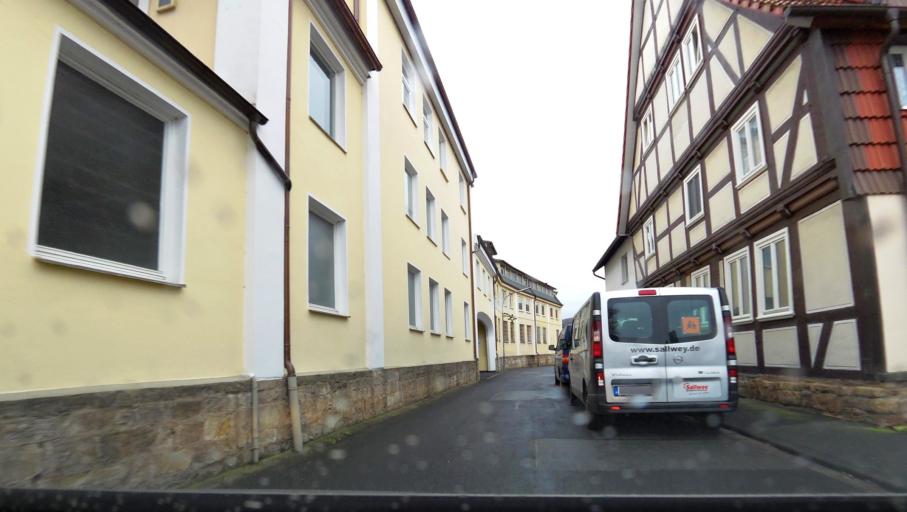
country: DE
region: Lower Saxony
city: Buhren
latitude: 51.4936
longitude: 9.6053
